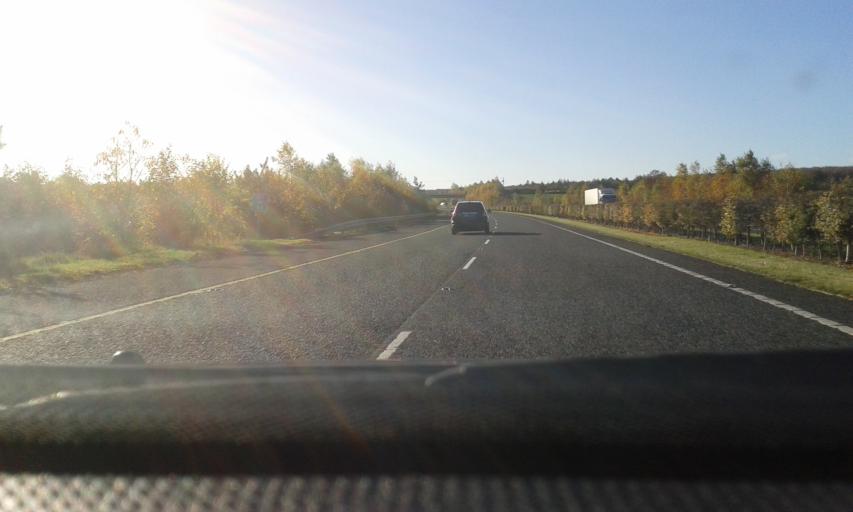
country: IE
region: Leinster
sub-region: Kildare
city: Monasterevin
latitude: 53.1368
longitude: -7.0341
